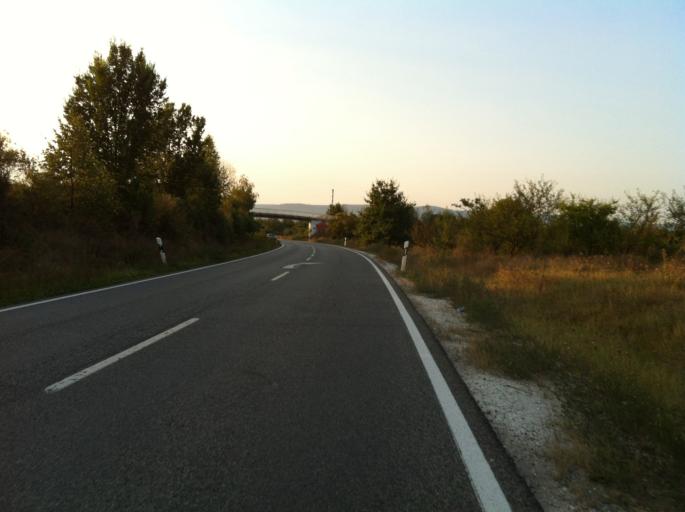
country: DE
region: Rheinland-Pfalz
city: Ingelheim am Rhein
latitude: 49.9654
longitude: 8.0494
